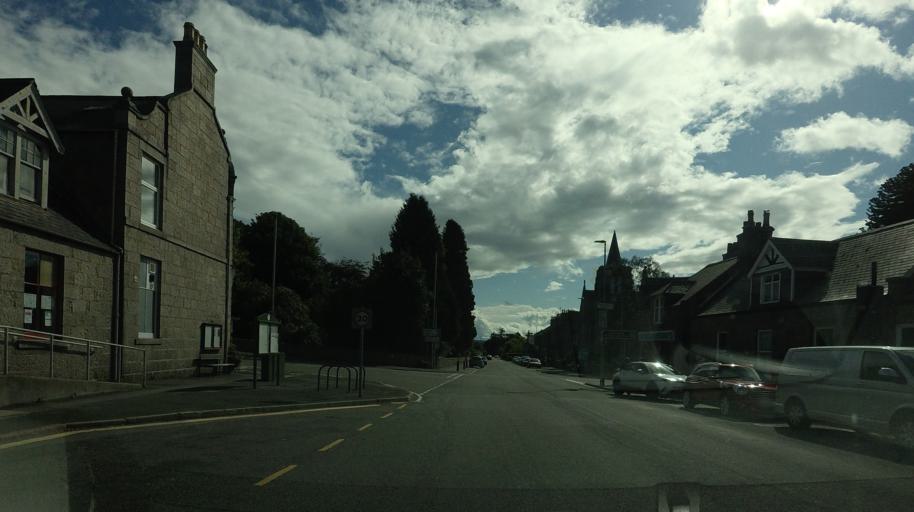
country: GB
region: Scotland
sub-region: Aberdeenshire
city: Torphins
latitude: 57.1053
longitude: -2.6234
